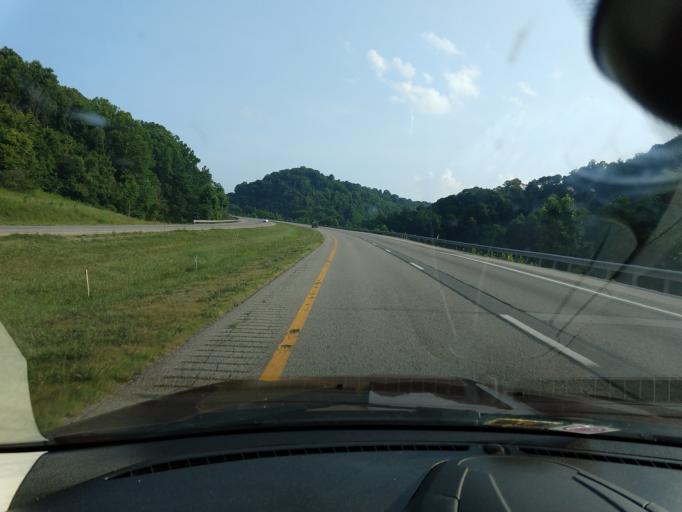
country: US
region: West Virginia
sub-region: Kanawha County
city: Charleston
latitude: 38.4355
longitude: -81.6258
